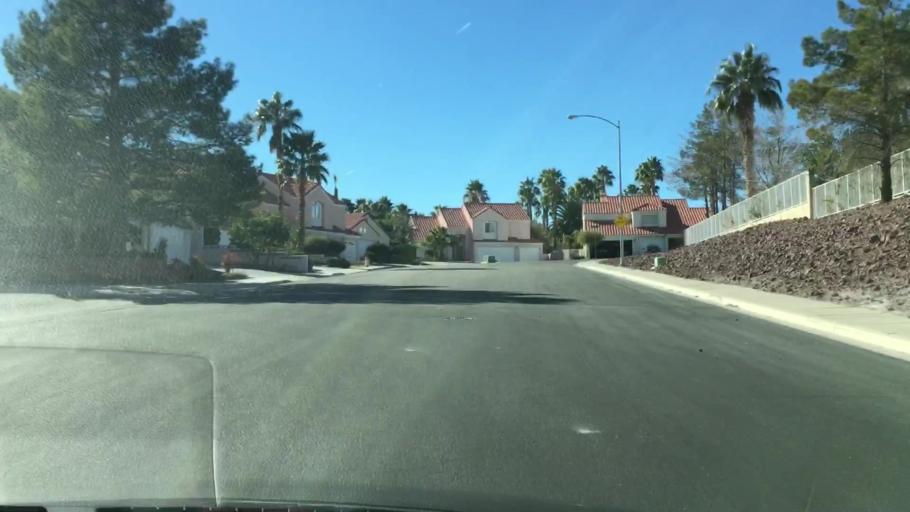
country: US
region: Nevada
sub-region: Clark County
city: Whitney
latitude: 36.0603
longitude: -115.0628
